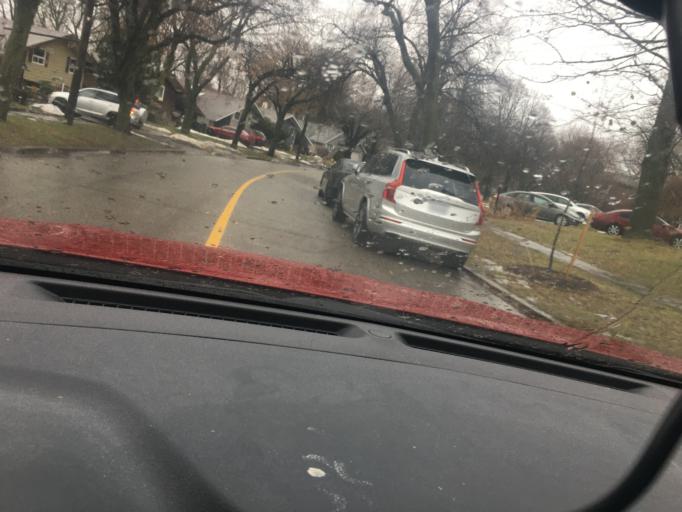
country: CA
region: Ontario
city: Scarborough
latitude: 43.7686
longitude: -79.2661
